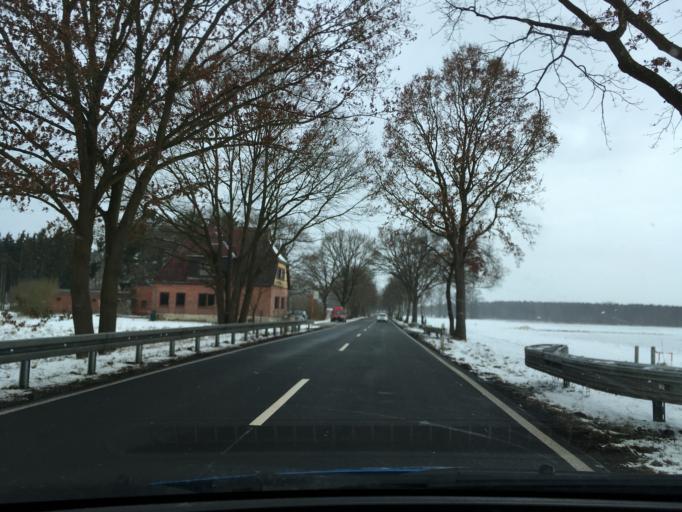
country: DE
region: Lower Saxony
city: Garstedt
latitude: 53.2944
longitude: 10.1940
